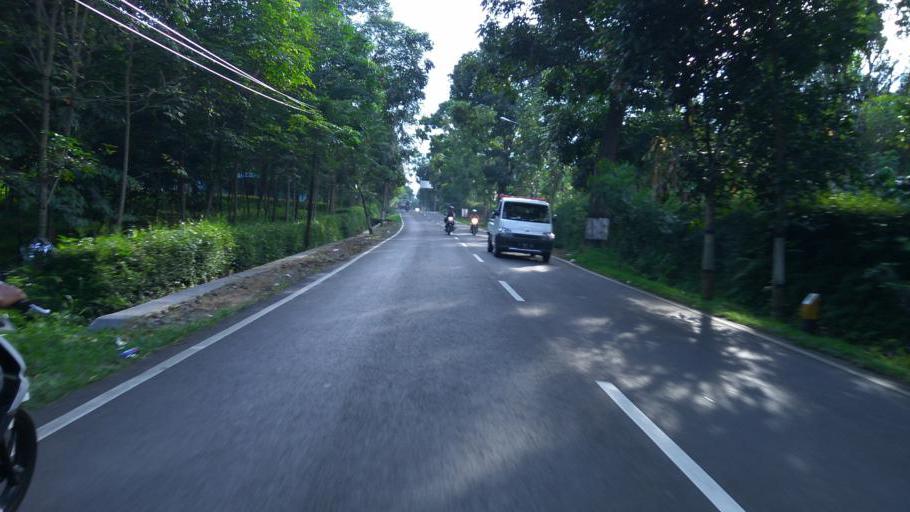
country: ID
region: Central Java
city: Salatiga
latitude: -7.3584
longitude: 110.4805
